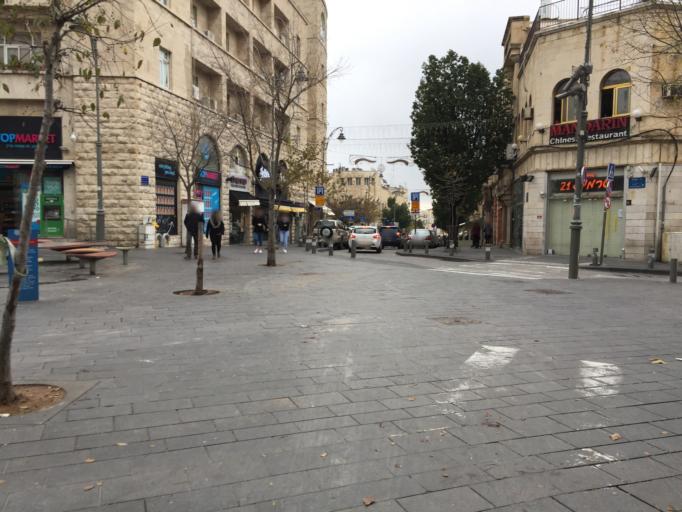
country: IL
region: Jerusalem
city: West Jerusalem
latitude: 31.7808
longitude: 35.2212
